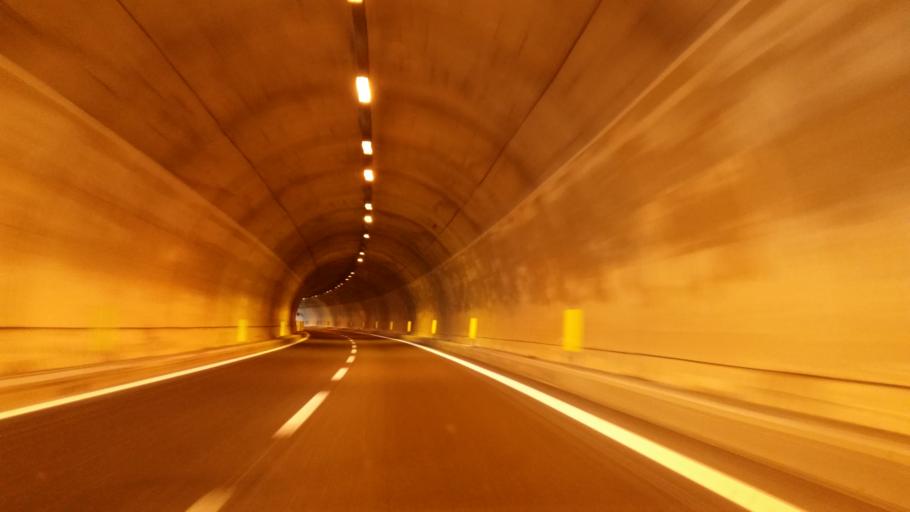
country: IT
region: Piedmont
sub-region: Provincia di Asti
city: Asti
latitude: 44.9135
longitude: 8.2431
